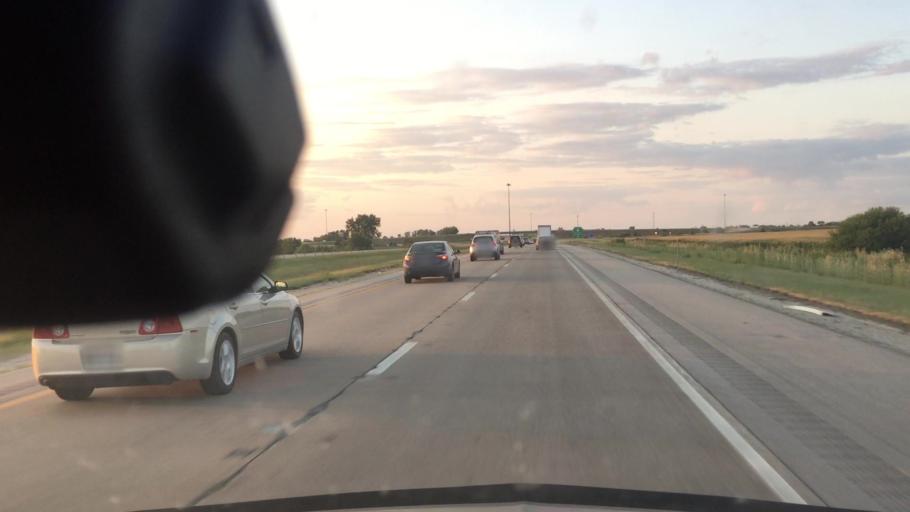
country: US
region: Illinois
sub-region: Livingston County
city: Dwight
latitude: 41.0854
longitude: -88.4516
